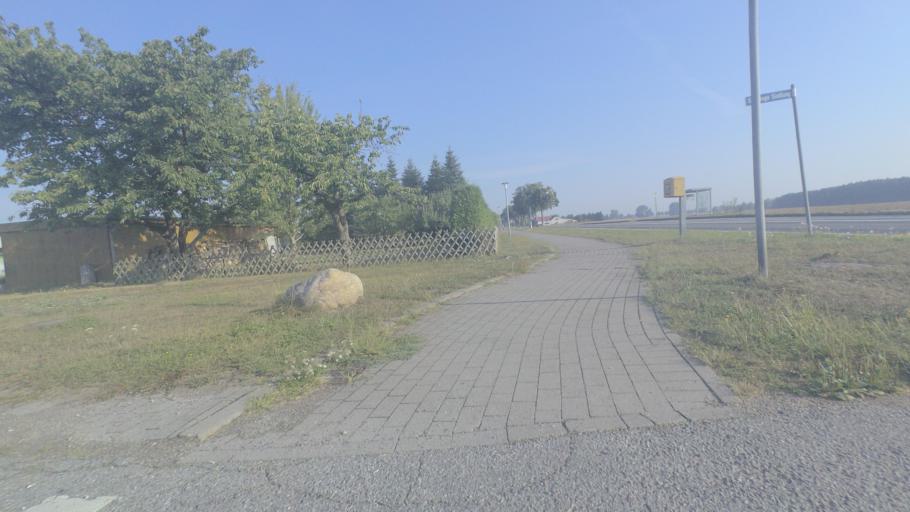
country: DE
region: Mecklenburg-Vorpommern
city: Gormin
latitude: 53.9864
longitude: 13.1516
